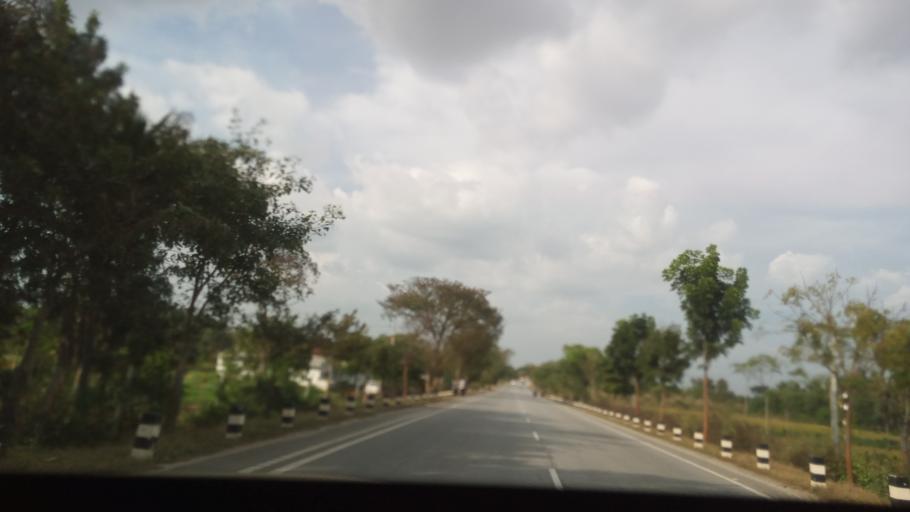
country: IN
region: Karnataka
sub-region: Tumkur
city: Kunigal
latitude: 12.8578
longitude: 77.0390
